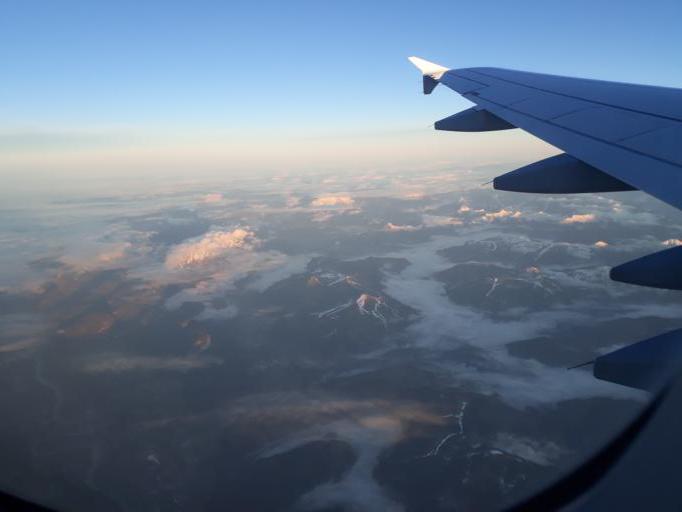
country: AT
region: Tyrol
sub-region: Politischer Bezirk Kufstein
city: Radfeld
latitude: 47.4311
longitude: 11.9381
